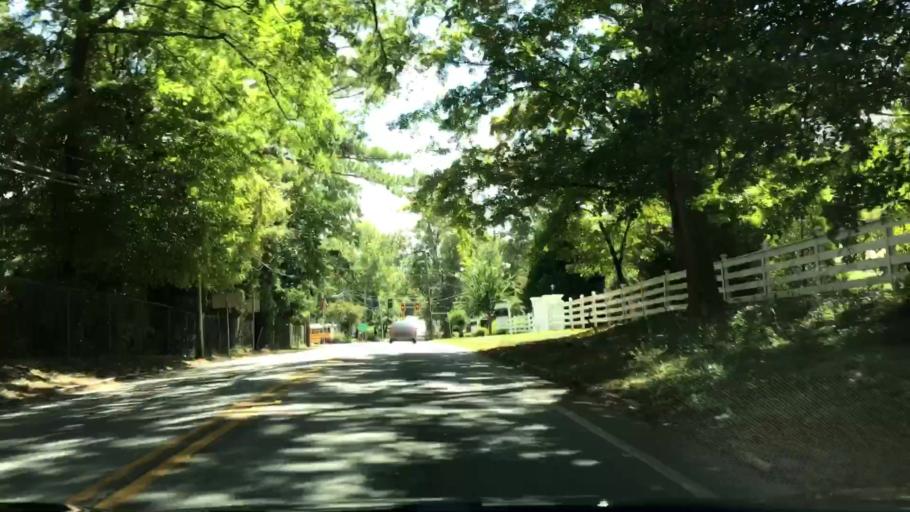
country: US
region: Georgia
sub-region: Greene County
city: Greensboro
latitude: 33.5772
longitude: -83.1880
